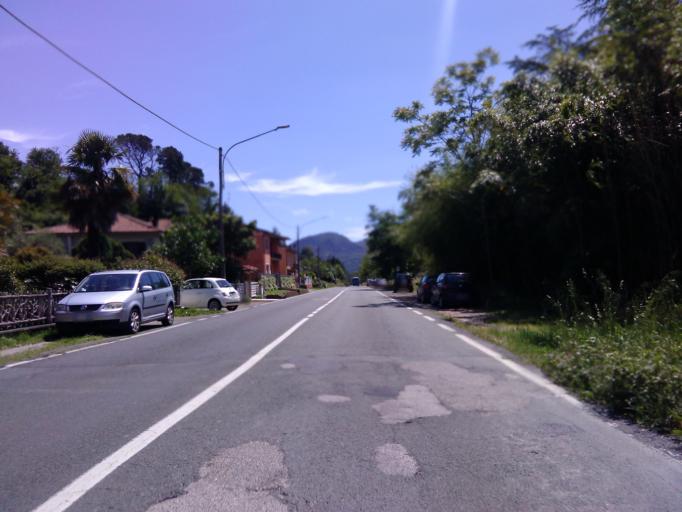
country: IT
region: Tuscany
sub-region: Provincia di Massa-Carrara
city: Terrarossa
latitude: 44.2378
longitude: 9.9599
